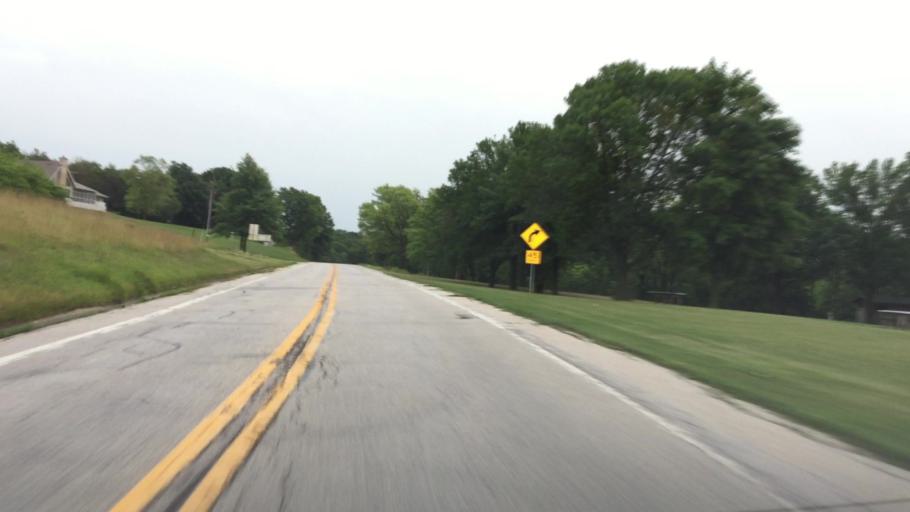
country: US
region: Illinois
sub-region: Hancock County
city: Nauvoo
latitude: 40.5197
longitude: -91.3631
